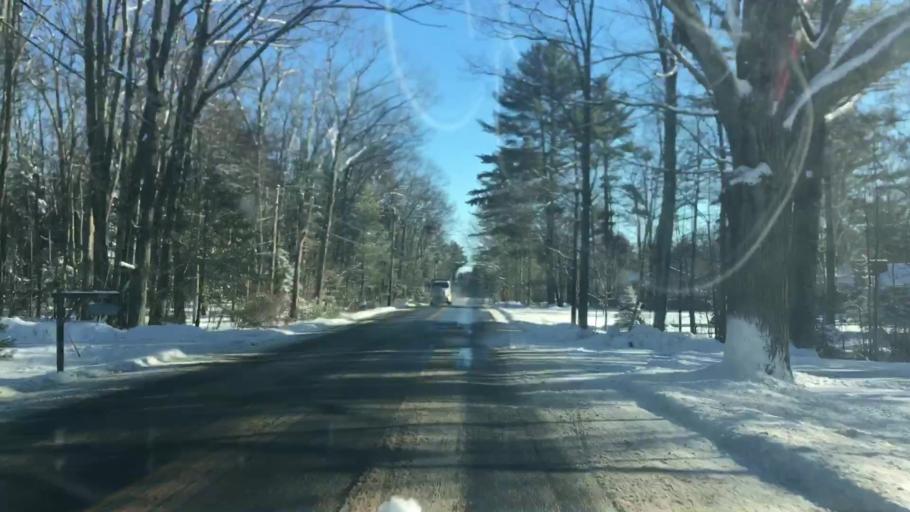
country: US
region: Maine
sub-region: Androscoggin County
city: Lisbon Falls
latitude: 43.9279
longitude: -70.0487
